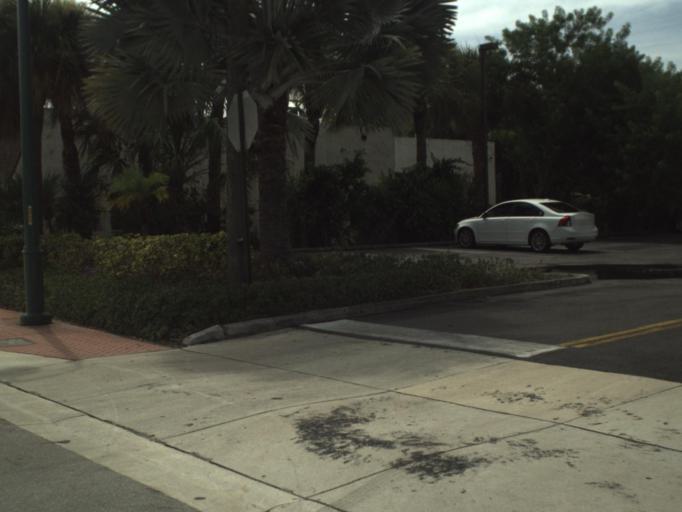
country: US
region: Florida
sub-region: Palm Beach County
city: Riviera Beach
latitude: 26.7833
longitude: -80.0519
